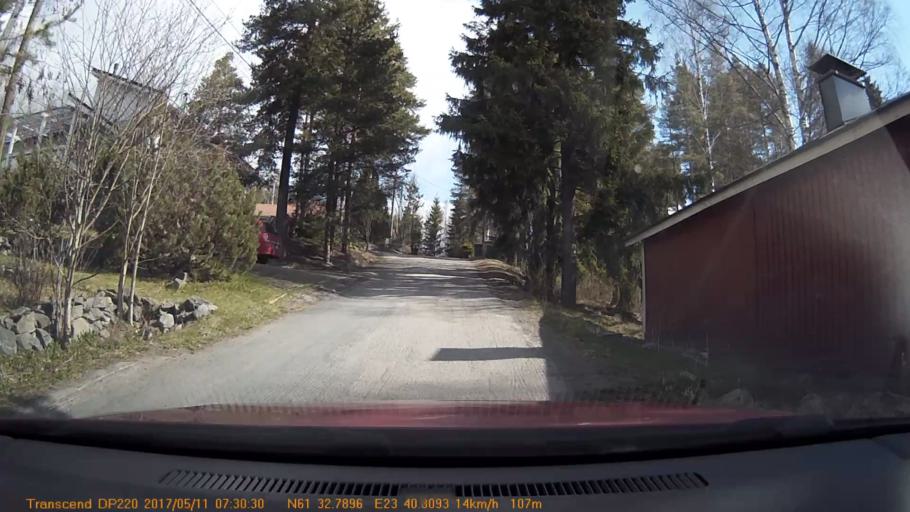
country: FI
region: Pirkanmaa
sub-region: Tampere
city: Yloejaervi
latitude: 61.5465
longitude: 23.6802
